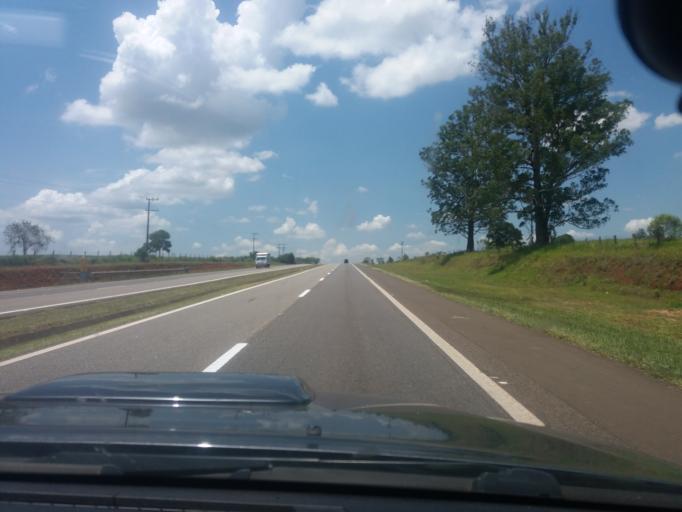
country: BR
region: Sao Paulo
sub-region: Itapetininga
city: Itapetininga
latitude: -23.5744
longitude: -47.9791
